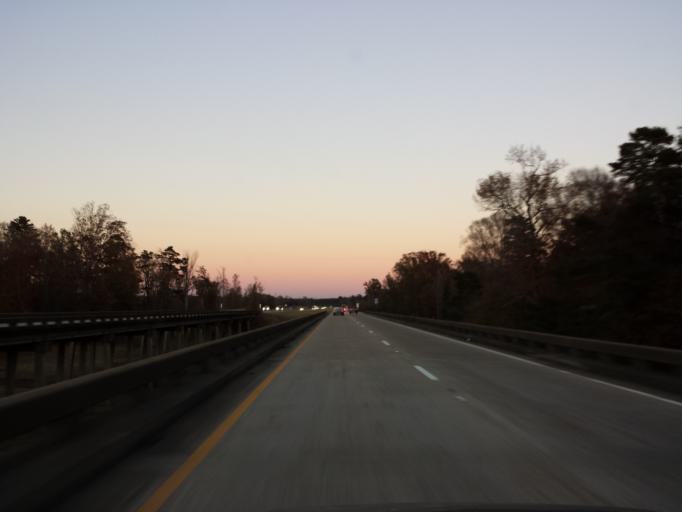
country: US
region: Mississippi
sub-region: Forrest County
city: Glendale
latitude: 31.5015
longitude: -89.3069
